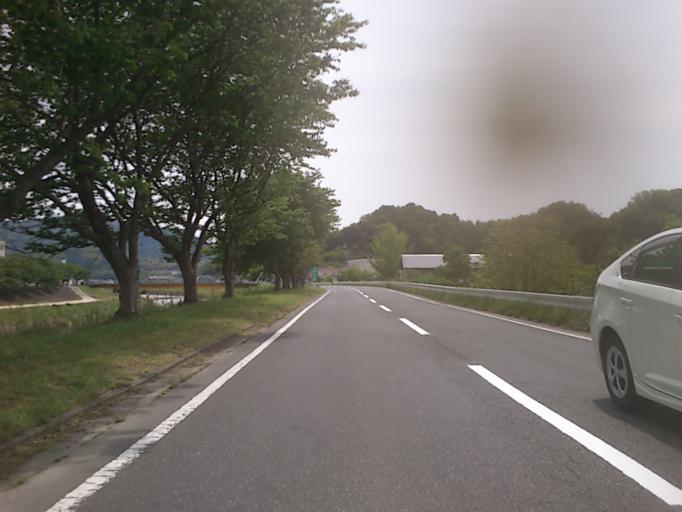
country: JP
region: Kyoto
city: Miyazu
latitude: 35.6616
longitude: 135.0867
